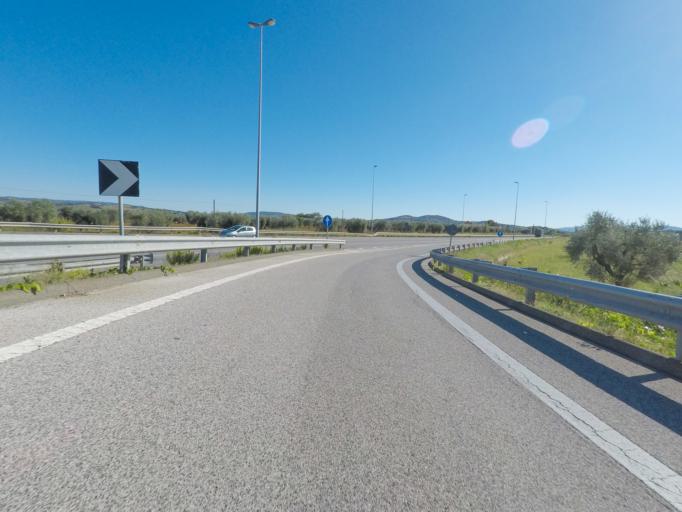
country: IT
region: Tuscany
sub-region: Provincia di Grosseto
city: Grosseto
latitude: 42.7718
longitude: 11.1458
